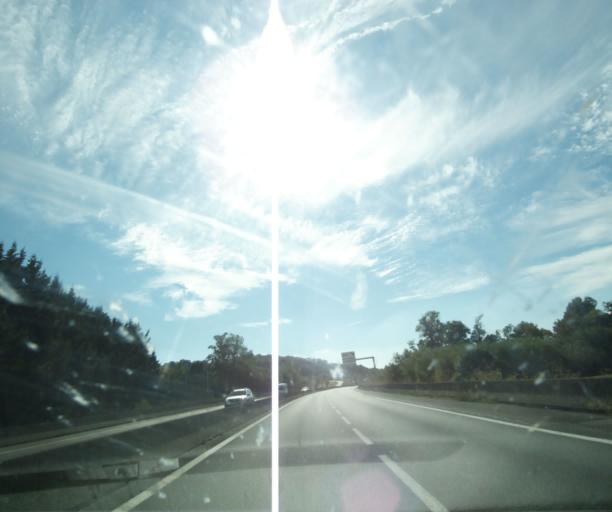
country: FR
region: Limousin
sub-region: Departement de la Correze
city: Ussac
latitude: 45.2050
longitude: 1.5145
